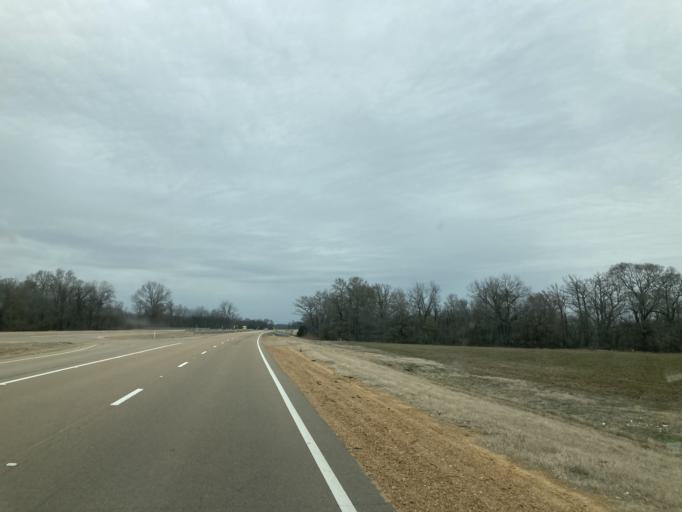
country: US
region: Mississippi
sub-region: Yazoo County
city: Yazoo City
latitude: 32.9967
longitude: -90.4695
